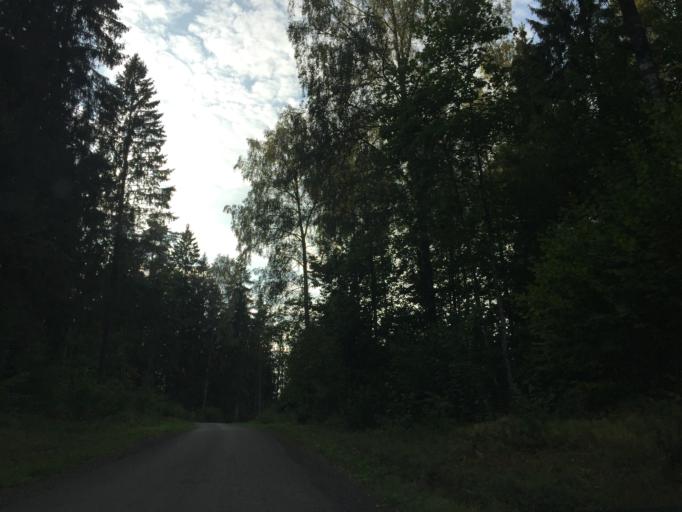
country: LV
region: Baldone
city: Baldone
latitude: 56.7728
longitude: 24.4179
